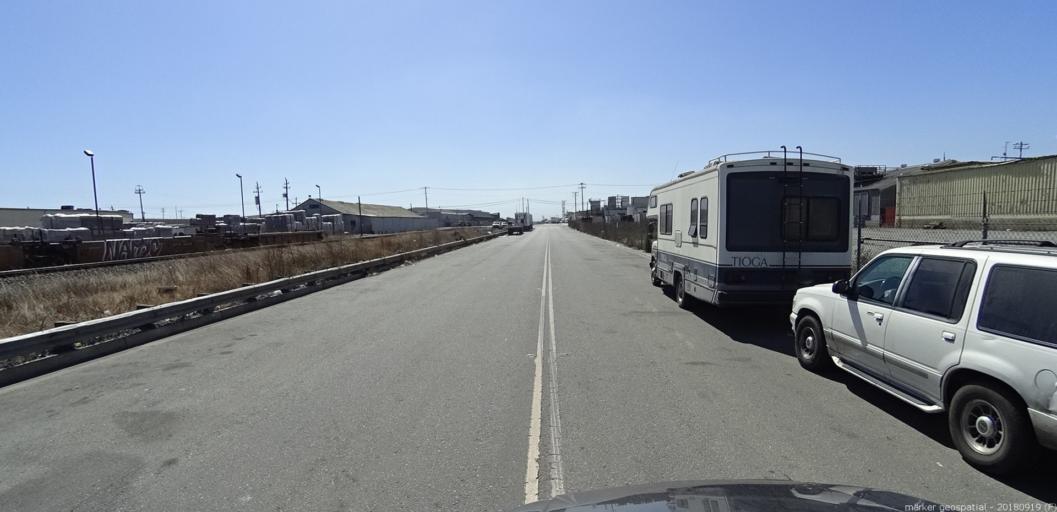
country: US
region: California
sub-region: Monterey County
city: Castroville
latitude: 36.7597
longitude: -121.7447
